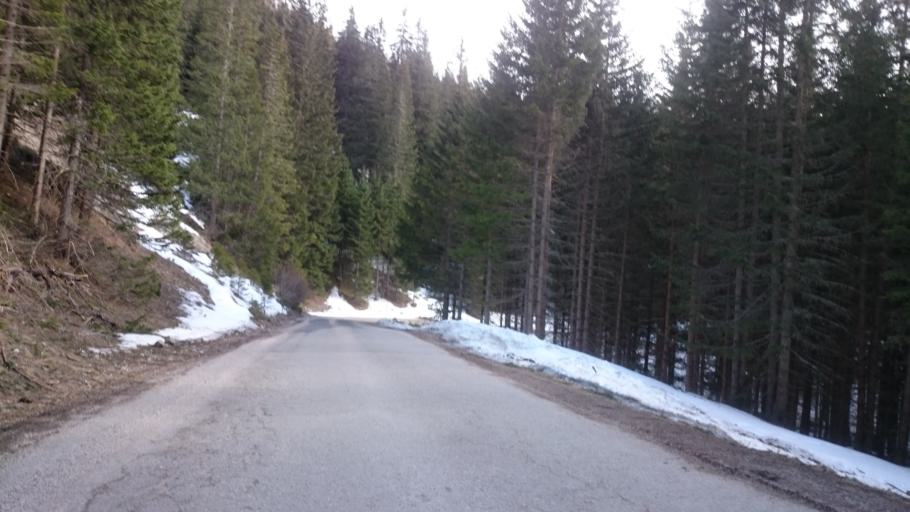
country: IT
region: Trentino-Alto Adige
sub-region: Bolzano
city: Braies
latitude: 46.6676
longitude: 12.1633
